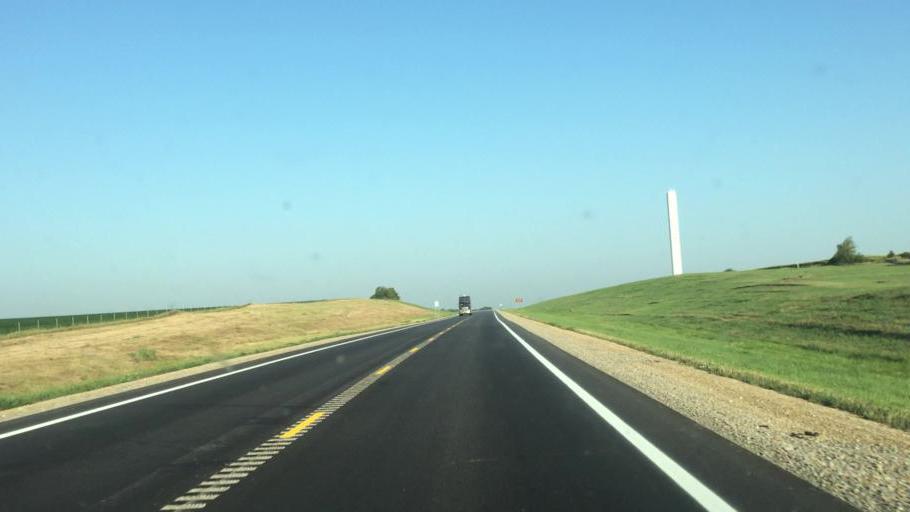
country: US
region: Kansas
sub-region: Doniphan County
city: Highland
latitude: 39.8422
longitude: -95.3446
